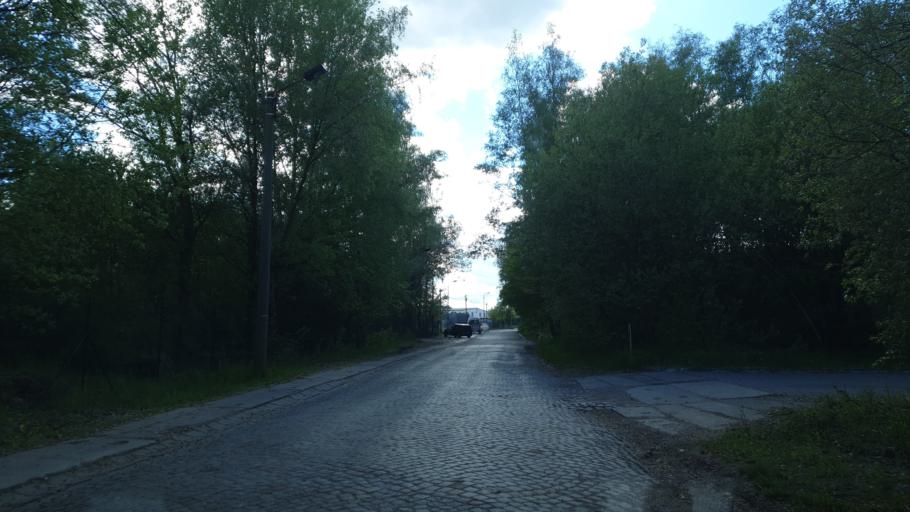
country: DE
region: Saxony
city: Gersdorf
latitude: 50.7472
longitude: 12.7002
